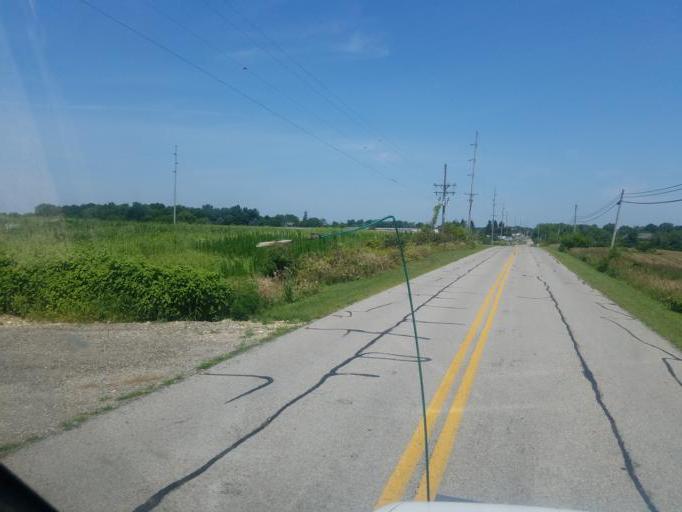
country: US
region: Ohio
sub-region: Logan County
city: West Liberty
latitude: 40.2622
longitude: -83.7587
